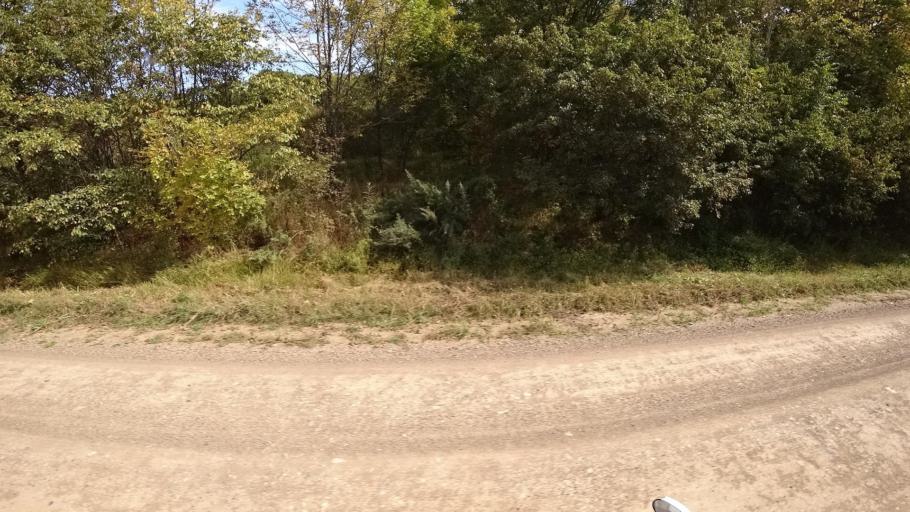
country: RU
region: Primorskiy
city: Yakovlevka
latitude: 44.7458
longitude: 133.6060
